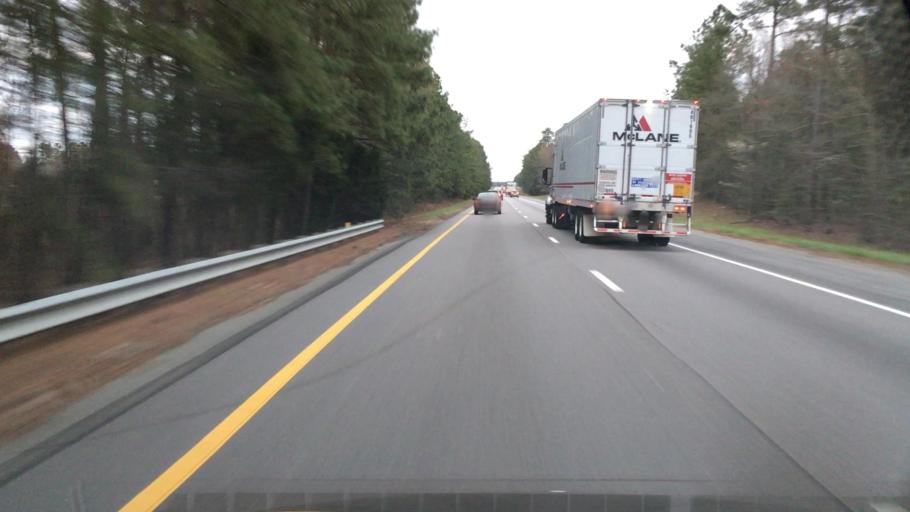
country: US
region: Virginia
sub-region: Sussex County
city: Sussex
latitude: 36.8453
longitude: -77.4354
